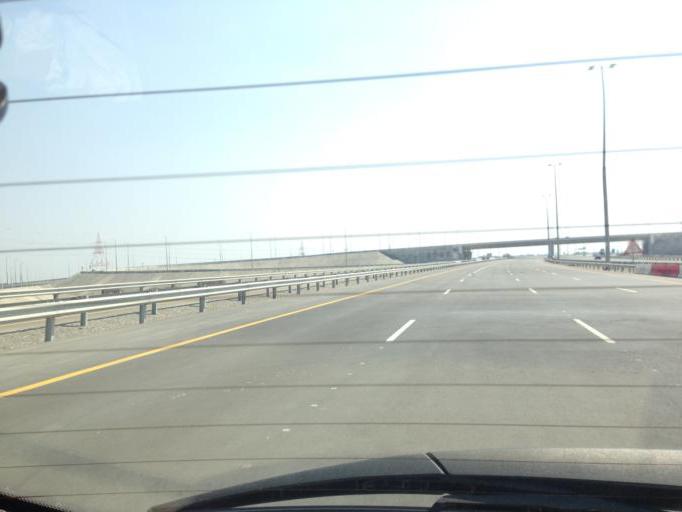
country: OM
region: Al Batinah
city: Barka'
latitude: 23.6333
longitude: 57.8692
